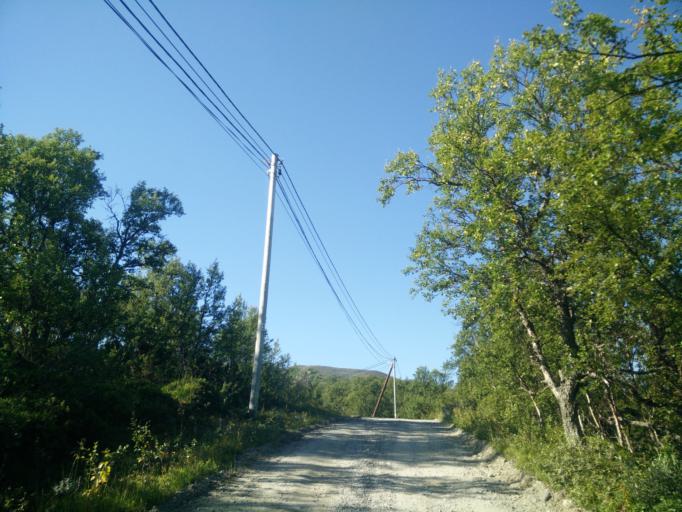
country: NO
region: Sor-Trondelag
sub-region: Tydal
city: Aas
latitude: 62.5769
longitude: 12.2024
